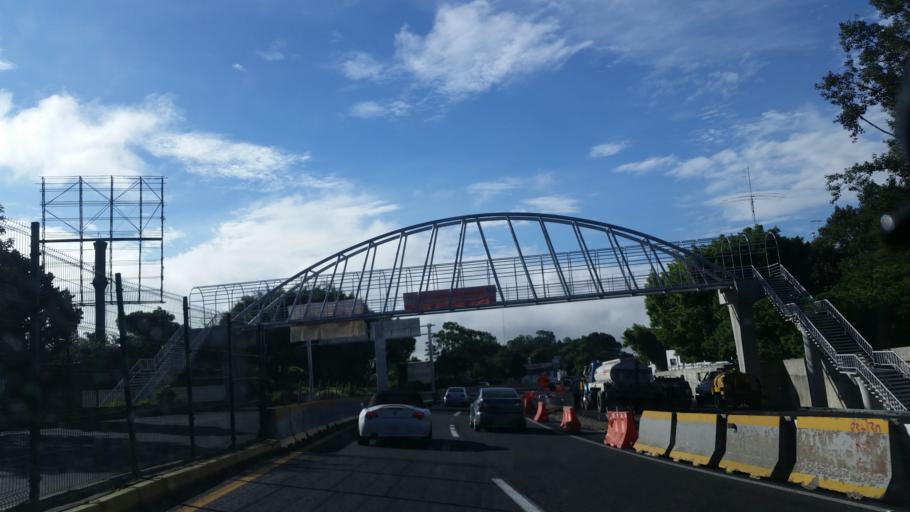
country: MX
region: Morelos
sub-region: Cuernavaca
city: Fraccionamiento Lomas de Ahuatlan
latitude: 18.9693
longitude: -99.2383
